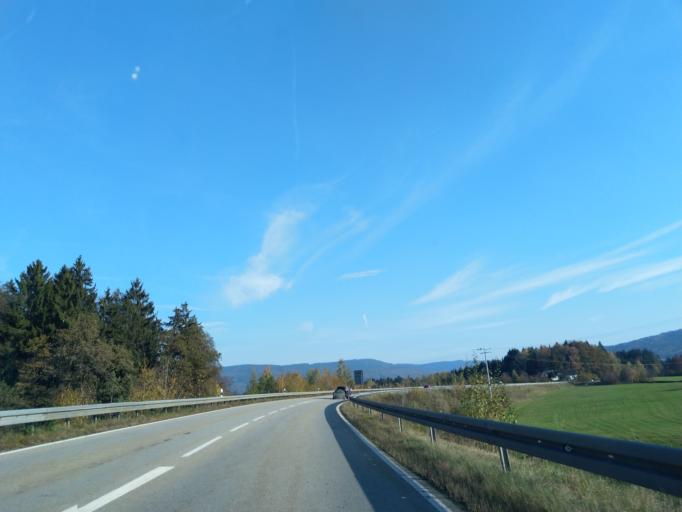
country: DE
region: Bavaria
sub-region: Lower Bavaria
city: Auerbach
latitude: 48.8154
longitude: 13.1207
